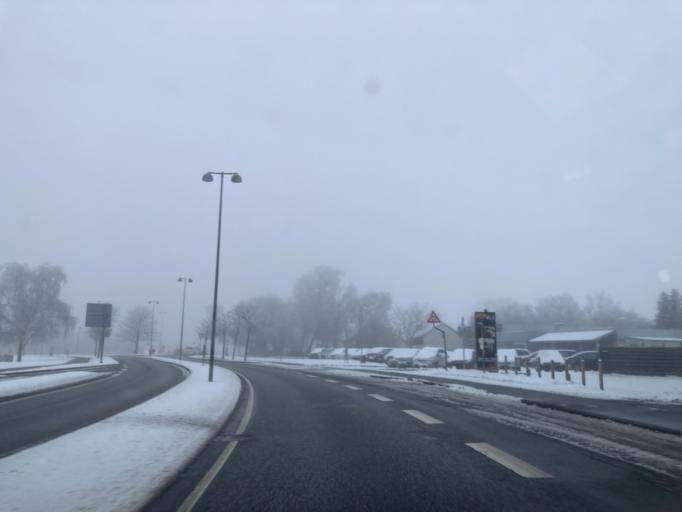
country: DK
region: Zealand
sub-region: Soro Kommune
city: Stenlille
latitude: 55.5885
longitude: 11.6584
